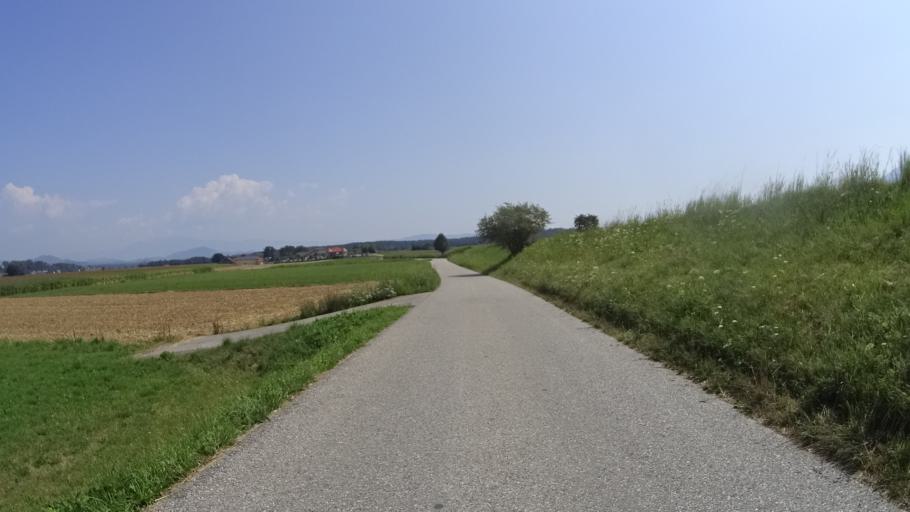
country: AT
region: Carinthia
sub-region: Politischer Bezirk Volkermarkt
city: Eberndorf
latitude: 46.5742
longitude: 14.6419
